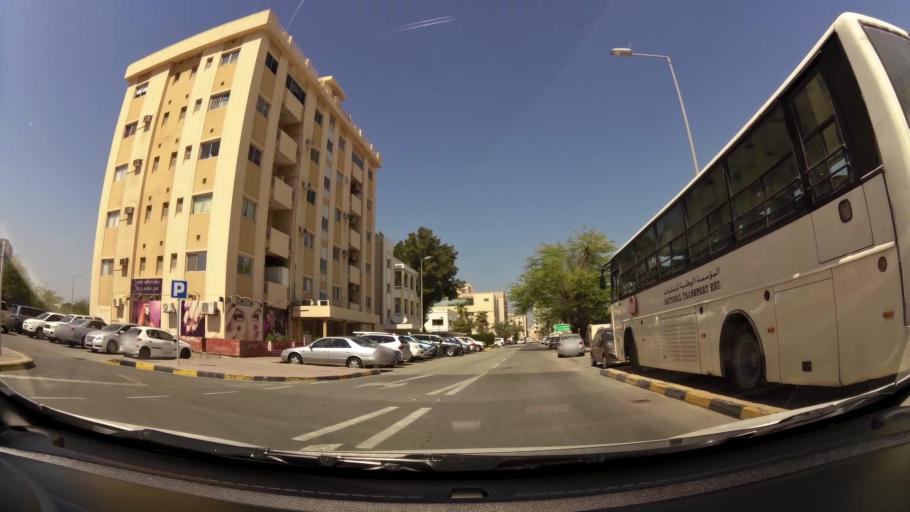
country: BH
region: Manama
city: Manama
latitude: 26.2206
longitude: 50.5914
